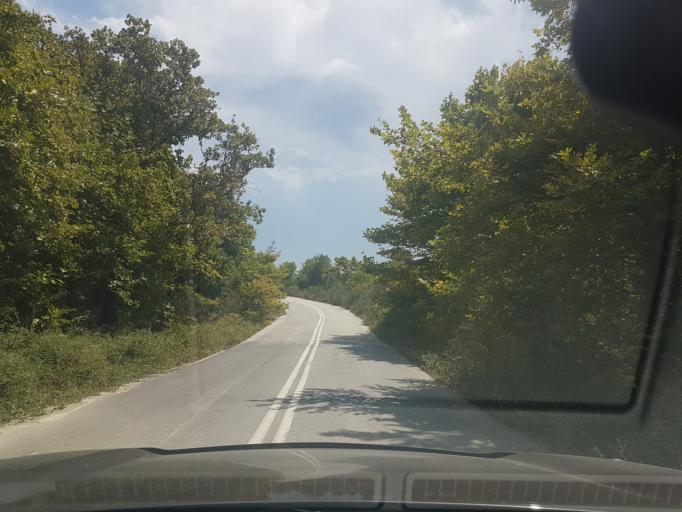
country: GR
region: Central Greece
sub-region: Nomos Evvoias
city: Kymi
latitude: 38.6467
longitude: 24.0487
